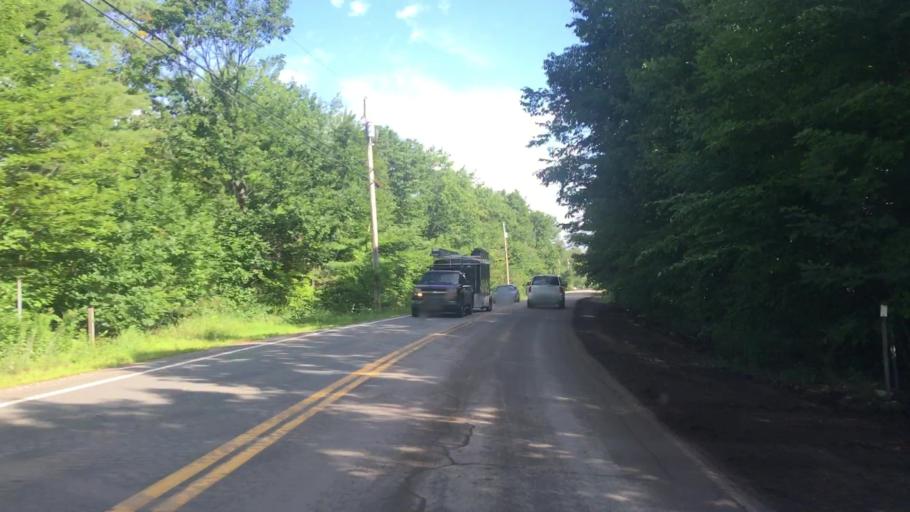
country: US
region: New Hampshire
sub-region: Belknap County
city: Gilford
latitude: 43.5305
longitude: -71.3459
